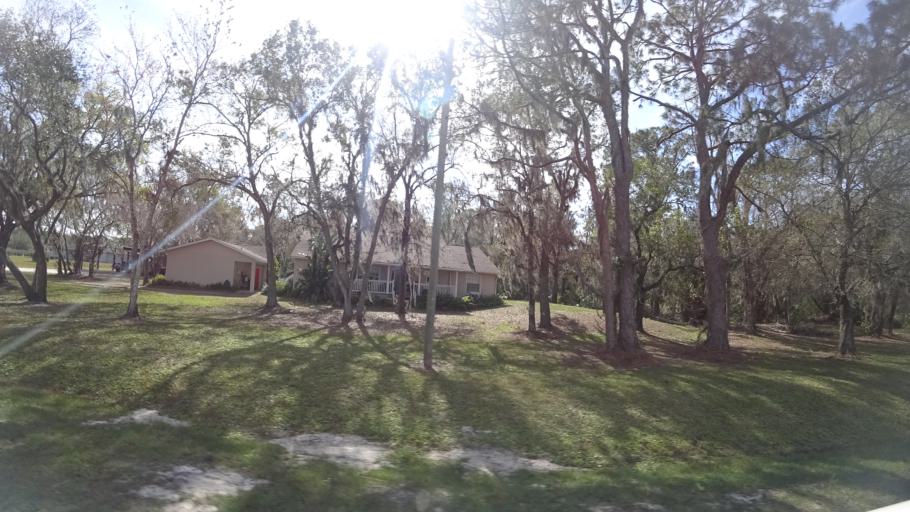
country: US
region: Florida
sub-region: Manatee County
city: Ellenton
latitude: 27.5759
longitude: -82.4198
